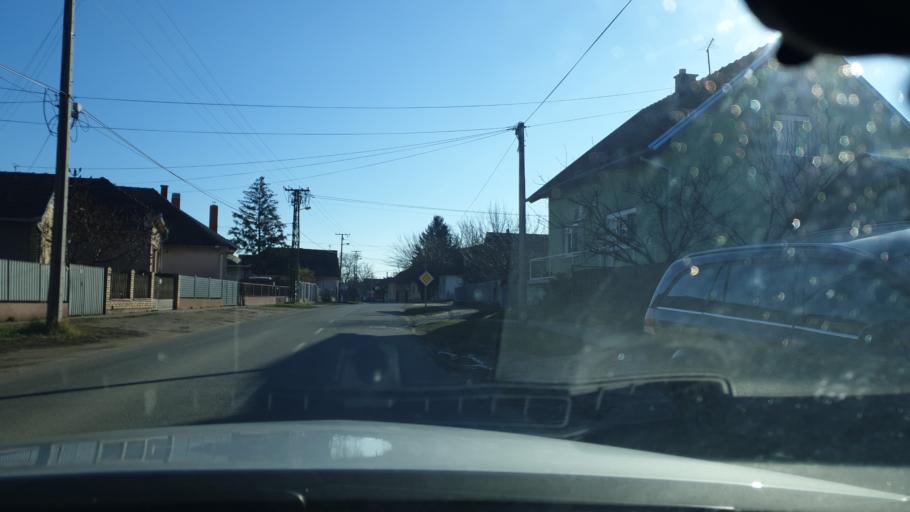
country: RS
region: Autonomna Pokrajina Vojvodina
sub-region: Sremski Okrug
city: Ruma
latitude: 45.0130
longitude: 19.8164
